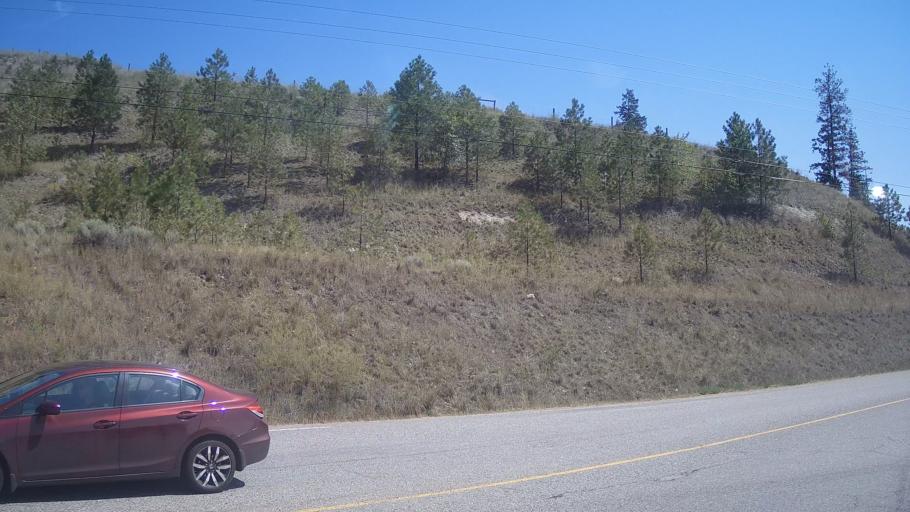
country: CA
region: British Columbia
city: Kamloops
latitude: 50.8616
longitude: -120.2649
